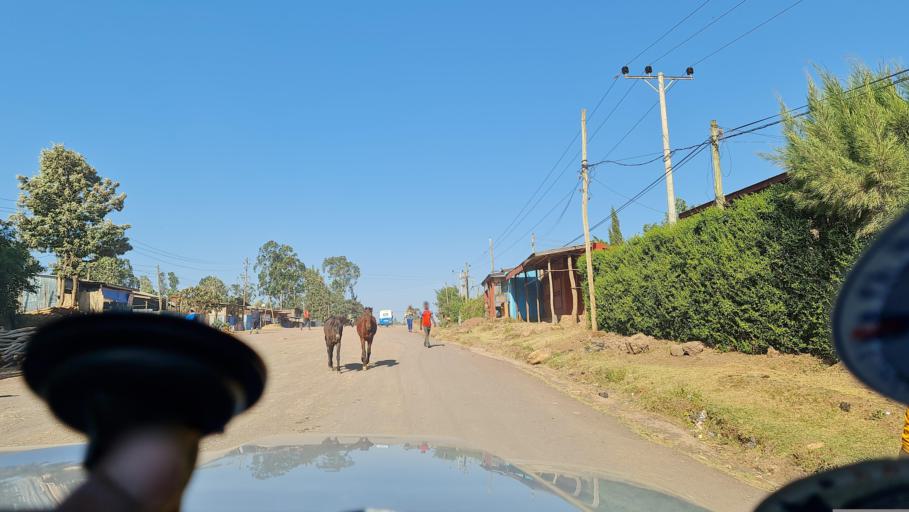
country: ET
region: Oromiya
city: Waliso
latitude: 8.5451
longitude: 37.9653
